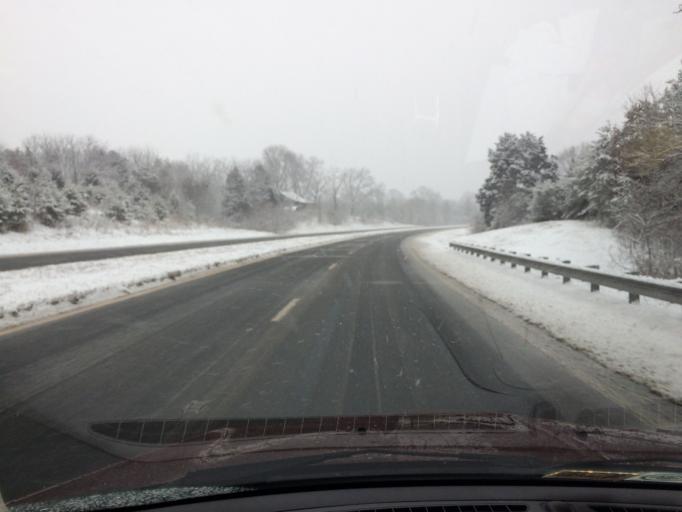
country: US
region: Virginia
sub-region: Amherst County
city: Madison Heights
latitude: 37.4687
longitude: -79.0985
